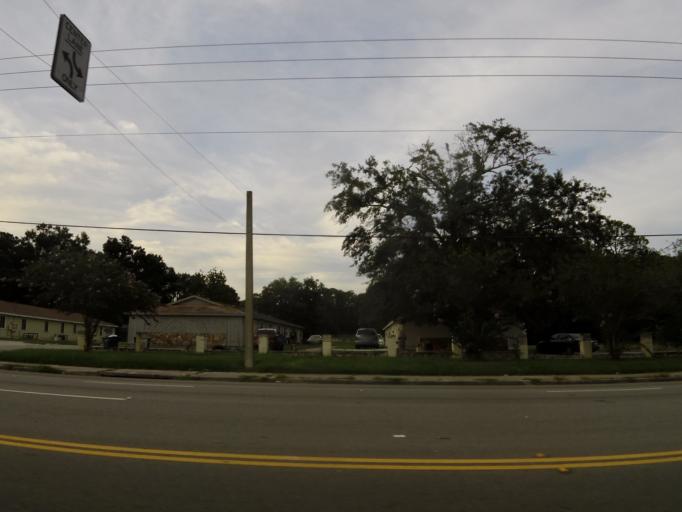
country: US
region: Florida
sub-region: Duval County
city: Jacksonville
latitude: 30.3873
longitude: -81.7151
